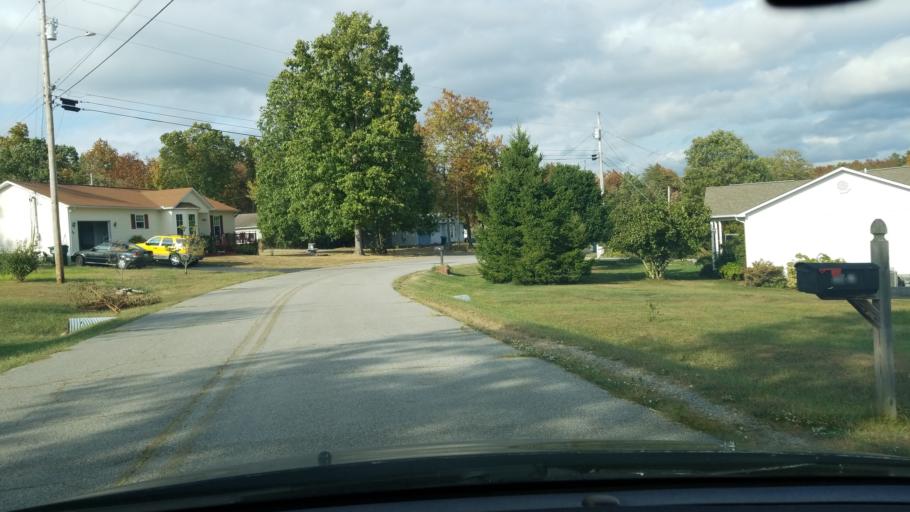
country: US
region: Tennessee
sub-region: Cumberland County
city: Crossville
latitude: 35.9467
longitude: -85.0506
